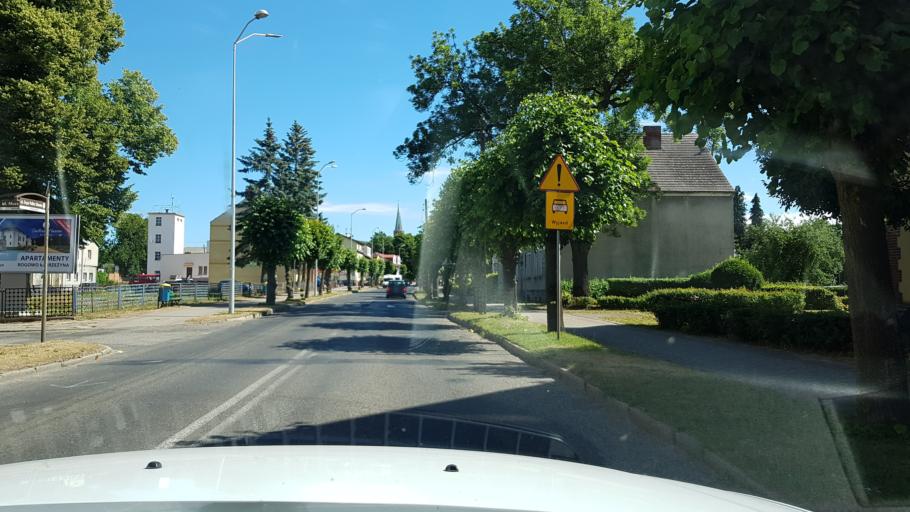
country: PL
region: West Pomeranian Voivodeship
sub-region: Powiat gryficki
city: Trzebiatow
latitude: 54.0588
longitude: 15.2617
